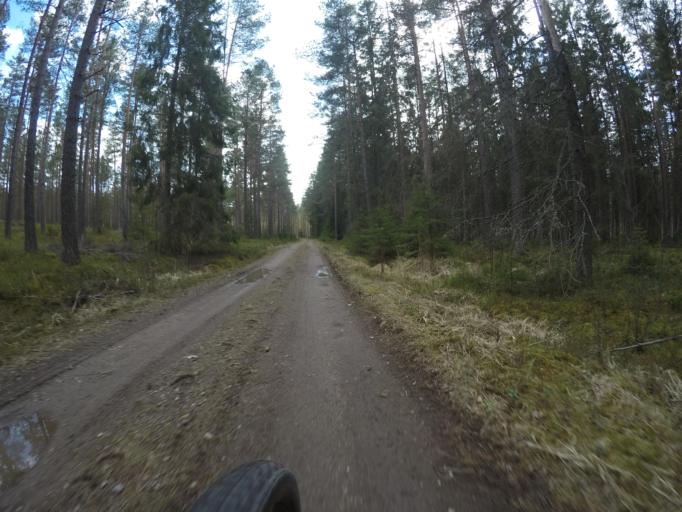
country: SE
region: Vaestmanland
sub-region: Kungsors Kommun
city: Kungsoer
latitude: 59.3403
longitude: 16.1071
